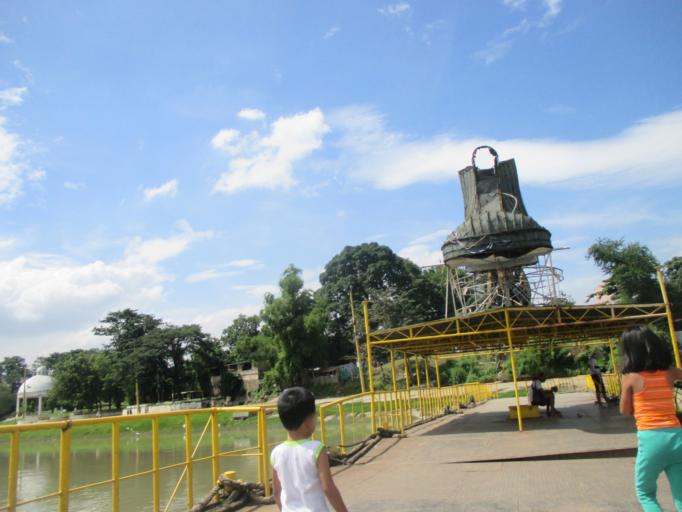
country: PH
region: Metro Manila
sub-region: Marikina
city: Calumpang
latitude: 14.6345
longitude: 121.0935
